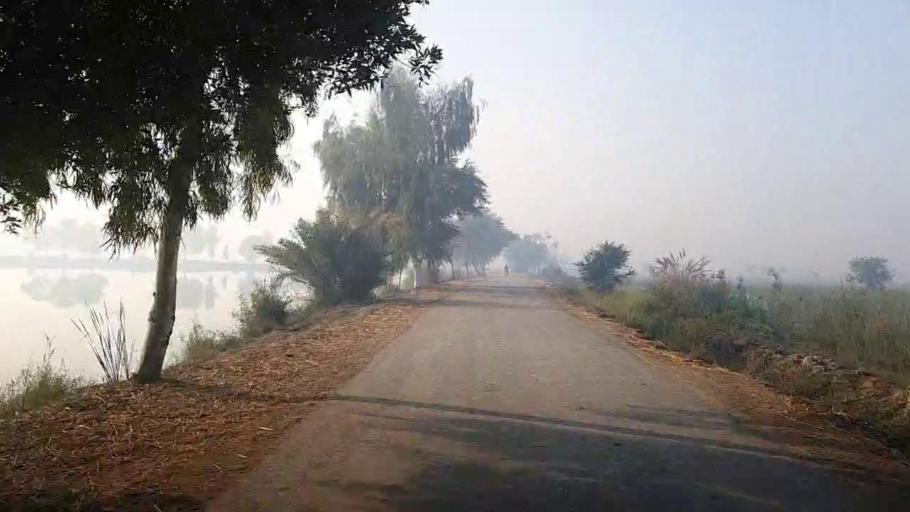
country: PK
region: Sindh
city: Mehar
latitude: 27.1493
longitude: 67.8235
